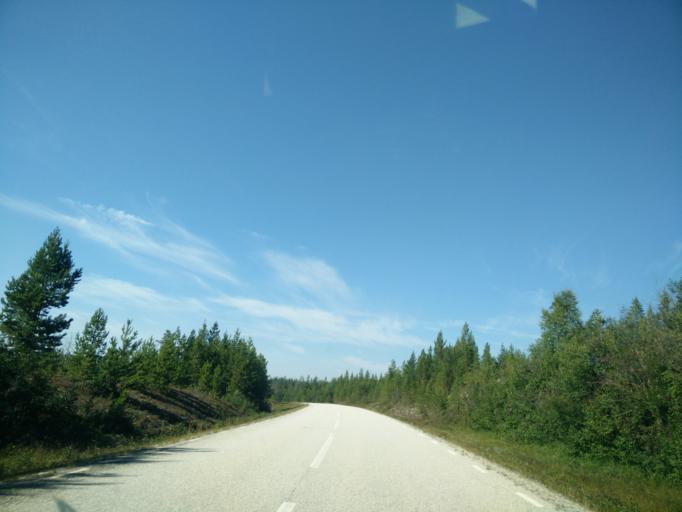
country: SE
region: Jaemtland
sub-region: Are Kommun
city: Jarpen
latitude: 62.8141
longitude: 13.5199
